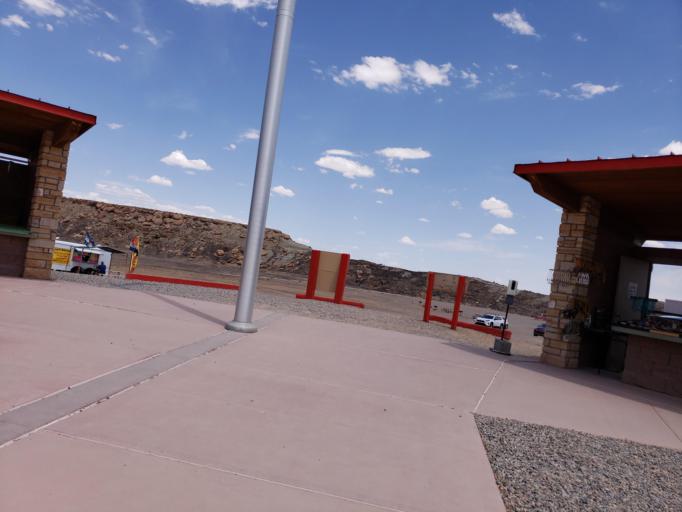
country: US
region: Colorado
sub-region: Montezuma County
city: Towaoc
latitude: 36.9990
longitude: -109.0449
